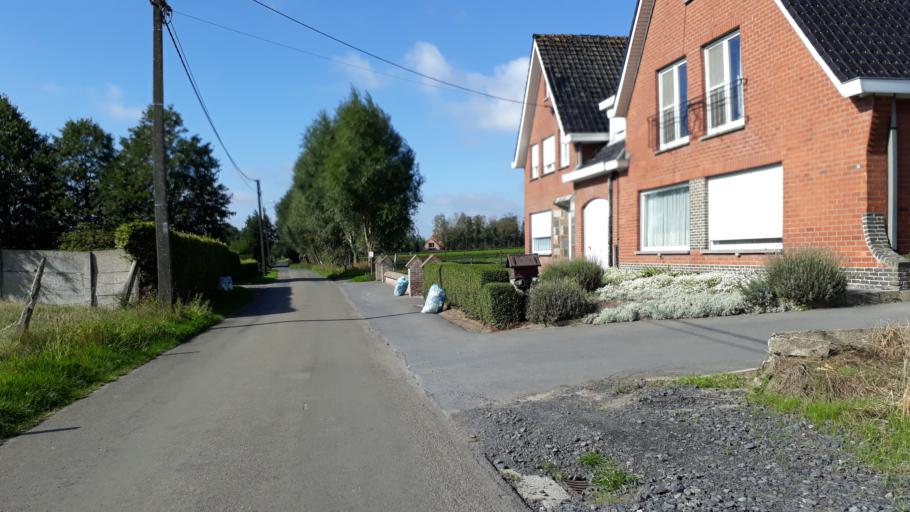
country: BE
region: Flanders
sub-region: Provincie West-Vlaanderen
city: Torhout
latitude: 51.0712
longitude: 3.1258
